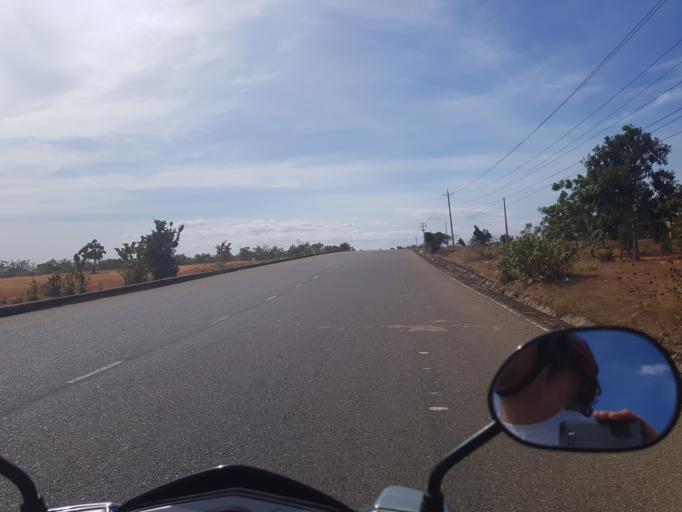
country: VN
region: Binh Thuan
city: Cho Lau
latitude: 11.0472
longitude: 108.3801
